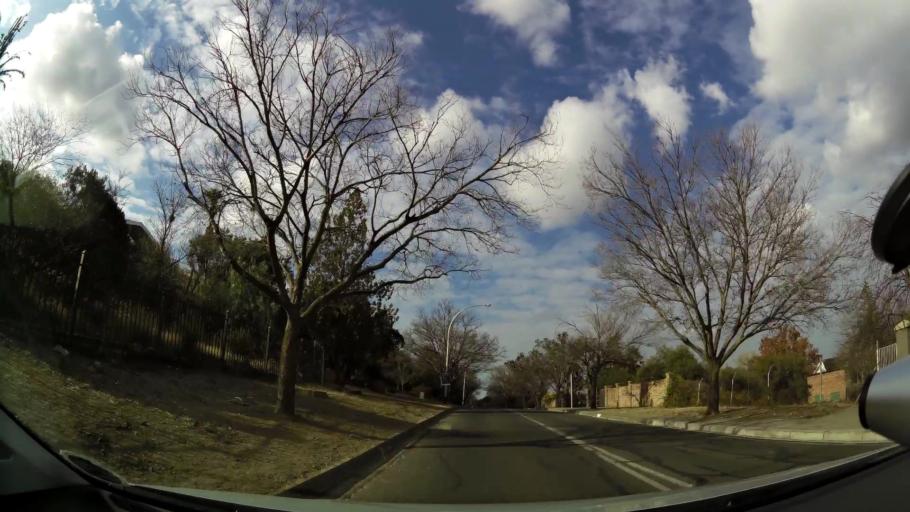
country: ZA
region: Orange Free State
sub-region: Mangaung Metropolitan Municipality
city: Bloemfontein
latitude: -29.0798
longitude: 26.2078
